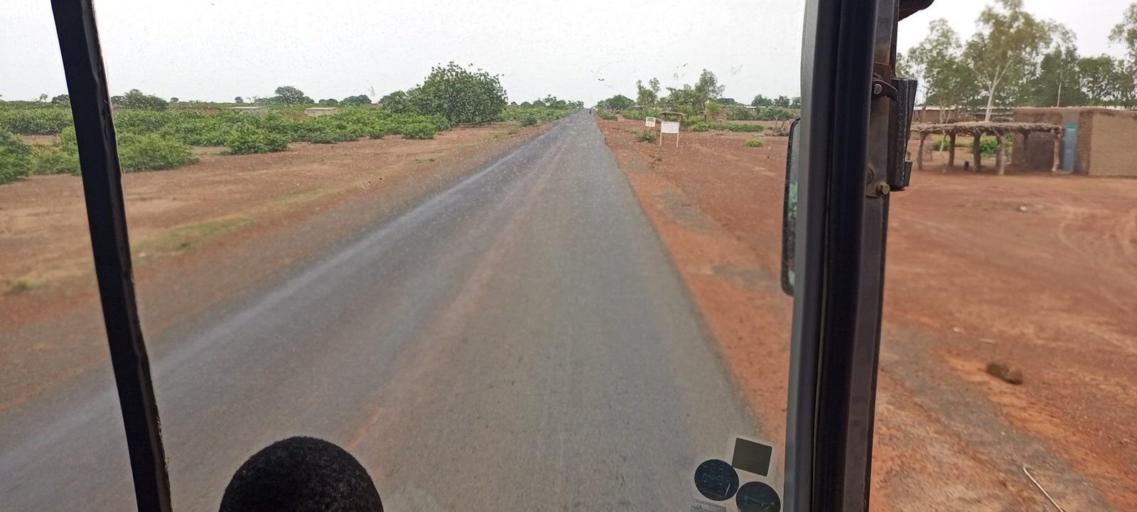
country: ML
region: Sikasso
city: Koutiala
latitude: 12.5394
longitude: -5.5743
